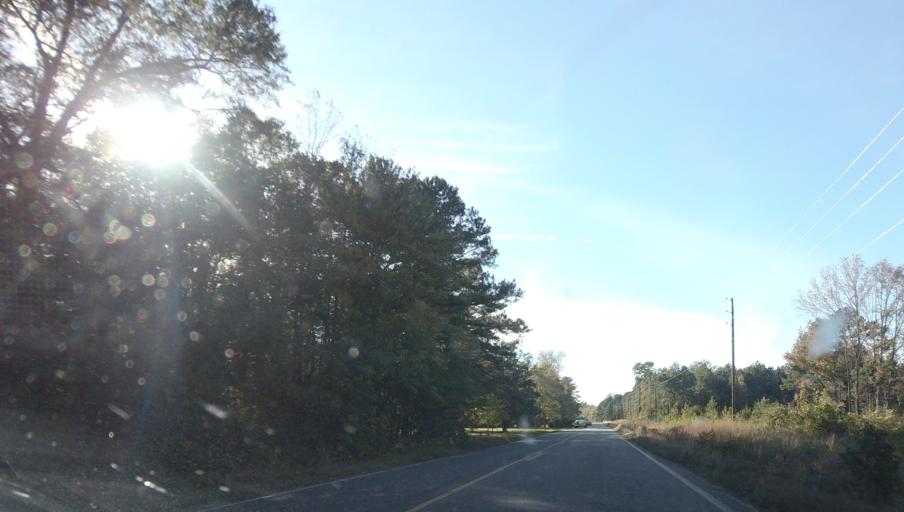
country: US
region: Georgia
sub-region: Talbot County
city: Sardis
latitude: 32.6900
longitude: -84.6818
